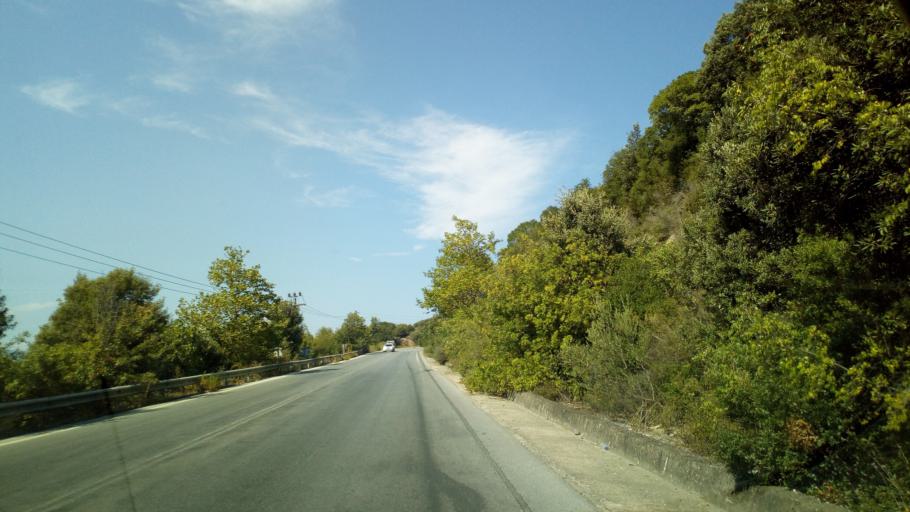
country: GR
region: Central Macedonia
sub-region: Nomos Thessalonikis
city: Stavros
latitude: 40.6557
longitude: 23.7332
